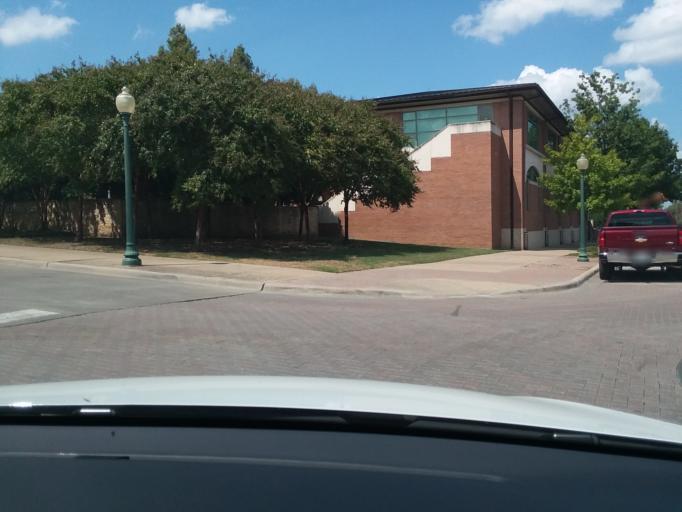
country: US
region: Texas
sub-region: Collin County
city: McKinney
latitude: 33.1993
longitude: -96.6151
